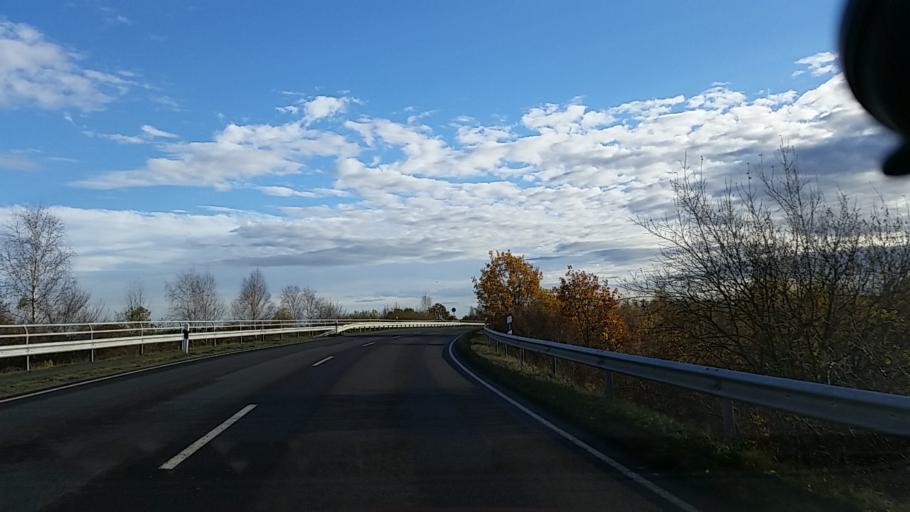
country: DE
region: Lower Saxony
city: Danndorf
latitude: 52.4322
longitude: 10.8685
